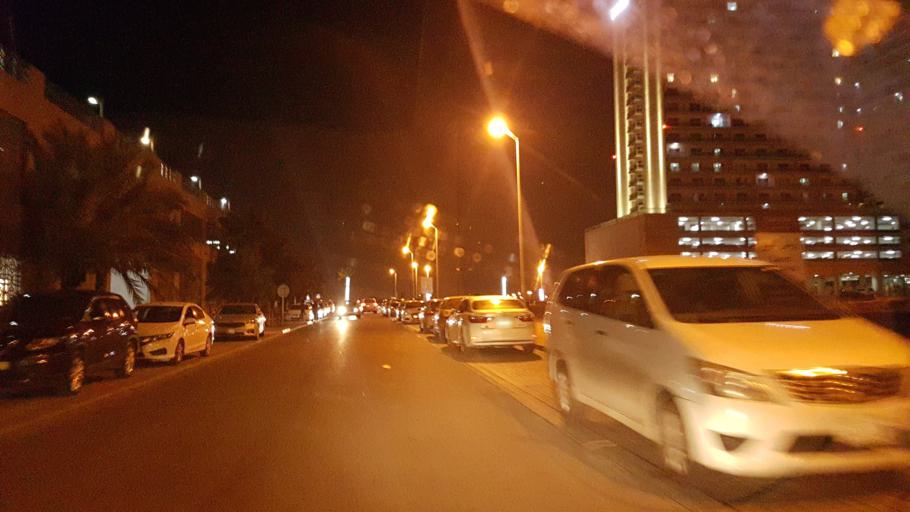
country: BH
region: Muharraq
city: Al Hadd
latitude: 26.2880
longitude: 50.6621
